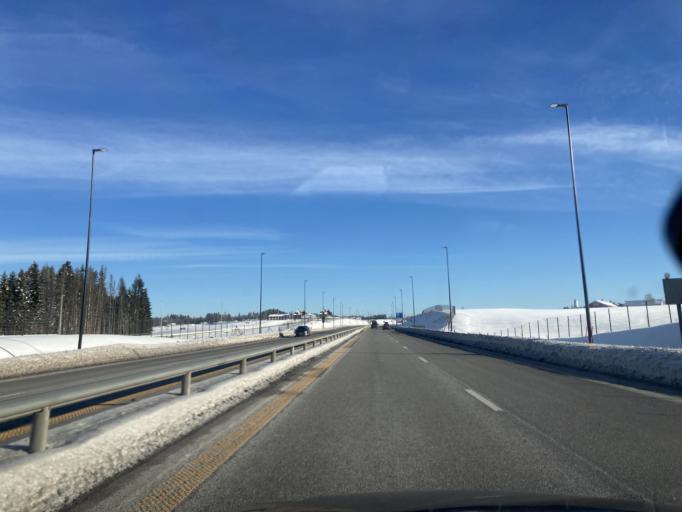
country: NO
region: Hedmark
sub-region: Loten
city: Loten
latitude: 60.8449
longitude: 11.3581
